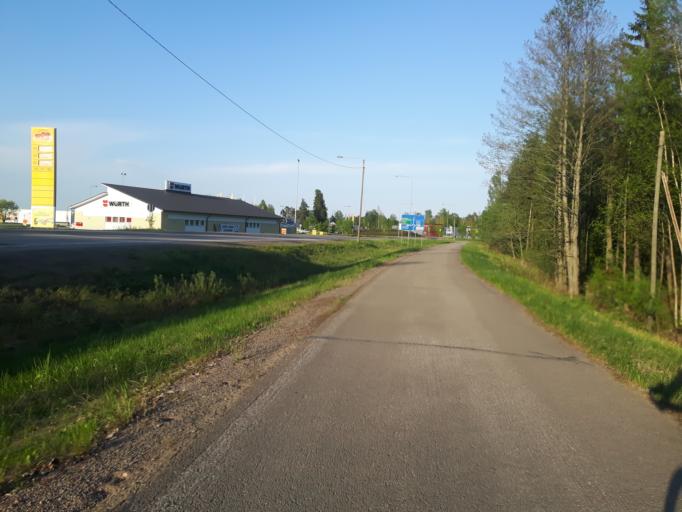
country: FI
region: Uusimaa
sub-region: Loviisa
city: Lovisa
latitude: 60.4580
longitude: 26.1908
